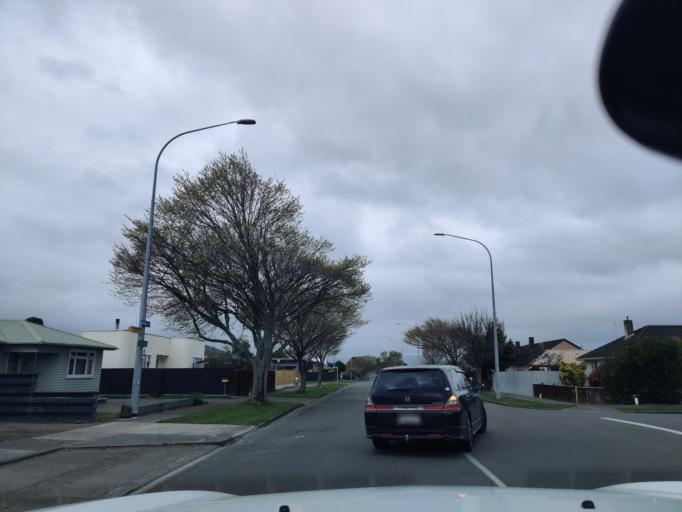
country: NZ
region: Manawatu-Wanganui
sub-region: Palmerston North City
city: Palmerston North
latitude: -40.3368
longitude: 175.6351
